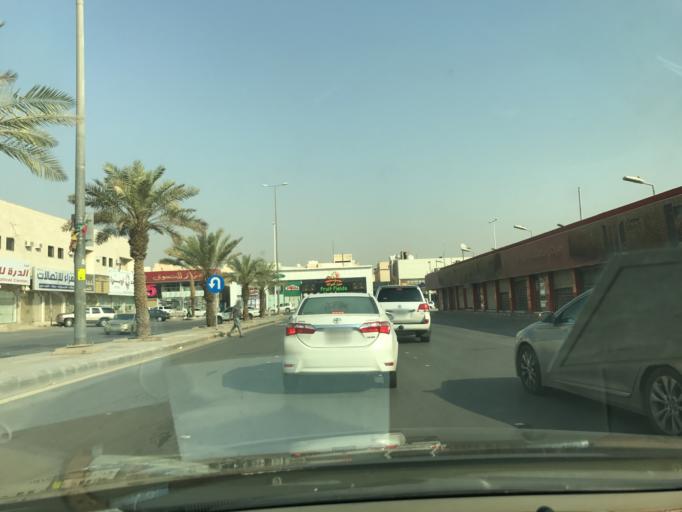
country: SA
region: Ar Riyad
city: Riyadh
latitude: 24.7437
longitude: 46.7567
